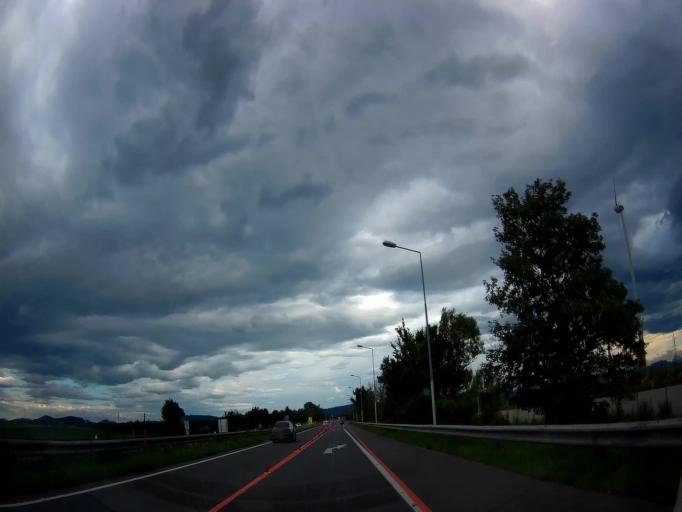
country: AT
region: Lower Austria
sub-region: Sankt Polten Stadt
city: Sankt Poelten
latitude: 48.1869
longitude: 15.6608
